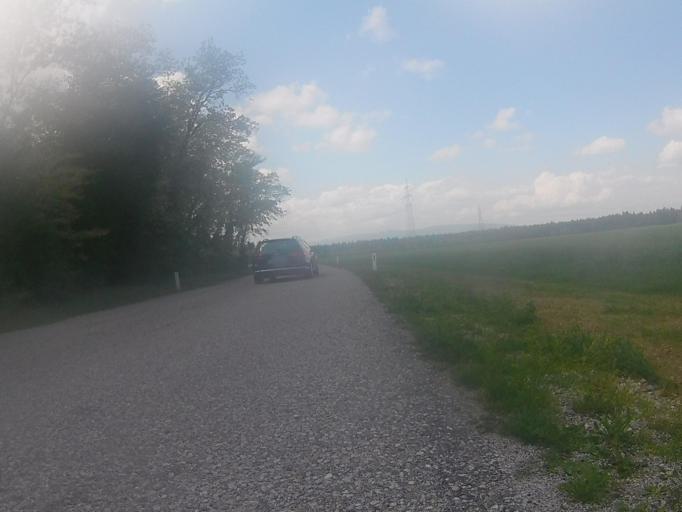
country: SI
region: Kidricevo
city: Kidricevo
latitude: 46.4262
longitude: 15.7781
